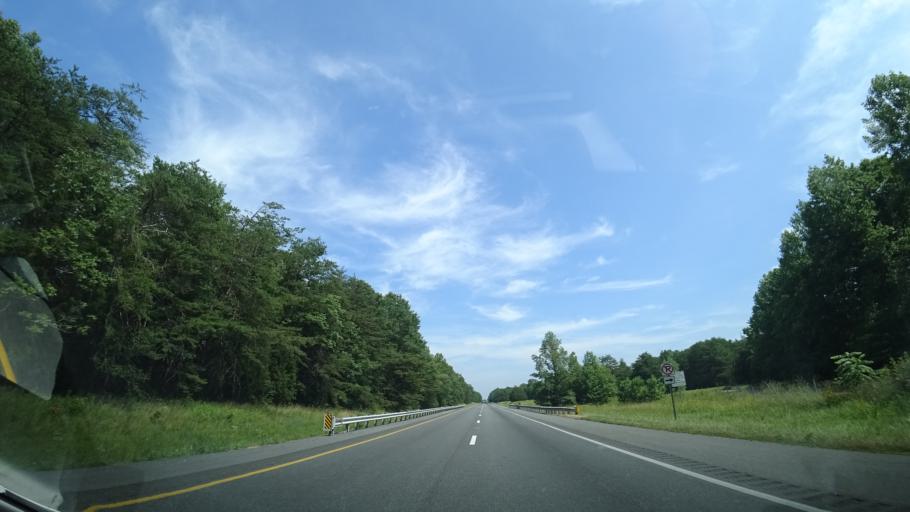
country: US
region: Virginia
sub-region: Louisa County
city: Louisa
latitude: 37.9127
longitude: -78.0675
